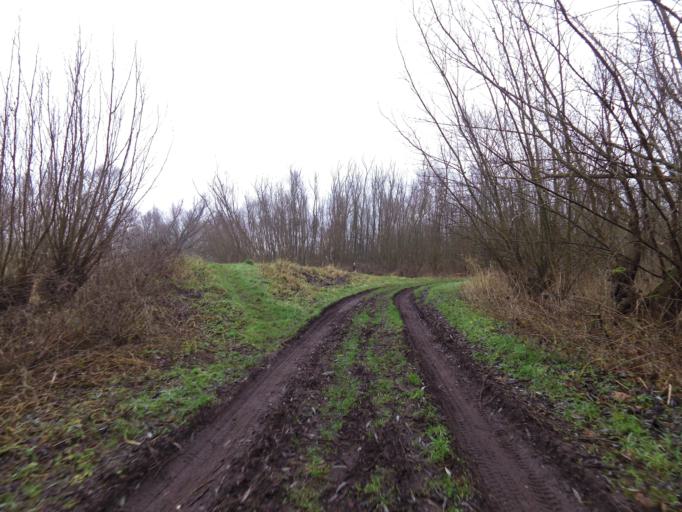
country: NL
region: South Holland
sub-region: Gemeente Oud-Beijerland
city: Oud-Beijerland
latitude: 51.8403
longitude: 4.3989
